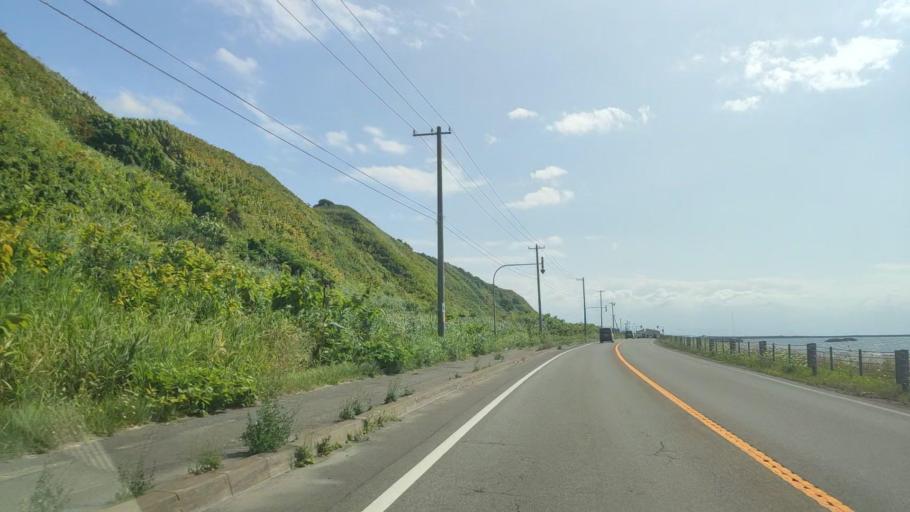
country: JP
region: Hokkaido
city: Rumoi
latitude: 43.9889
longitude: 141.6505
